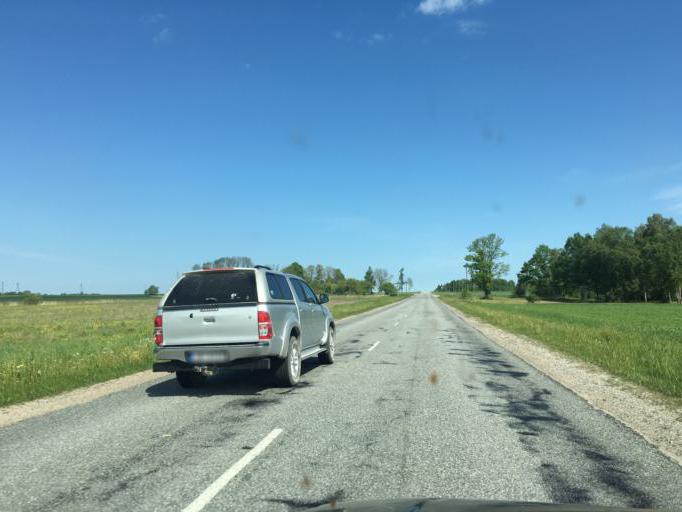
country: LV
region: Talsu Rajons
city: Valdemarpils
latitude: 57.3550
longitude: 22.4948
